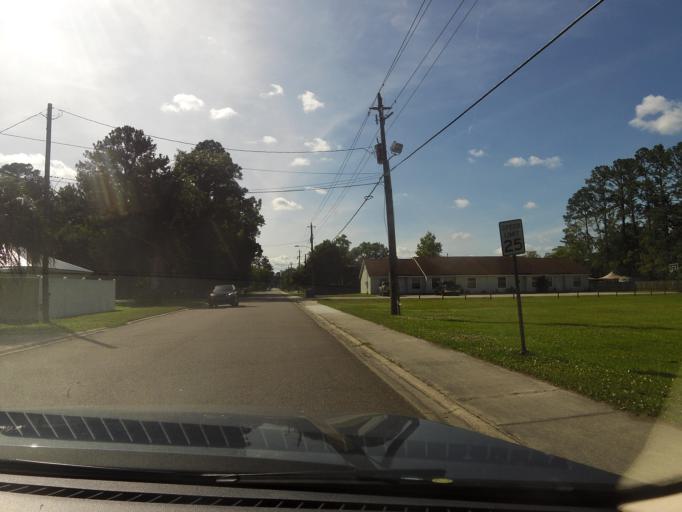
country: US
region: Florida
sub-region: Nassau County
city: Callahan
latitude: 30.5581
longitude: -81.8283
